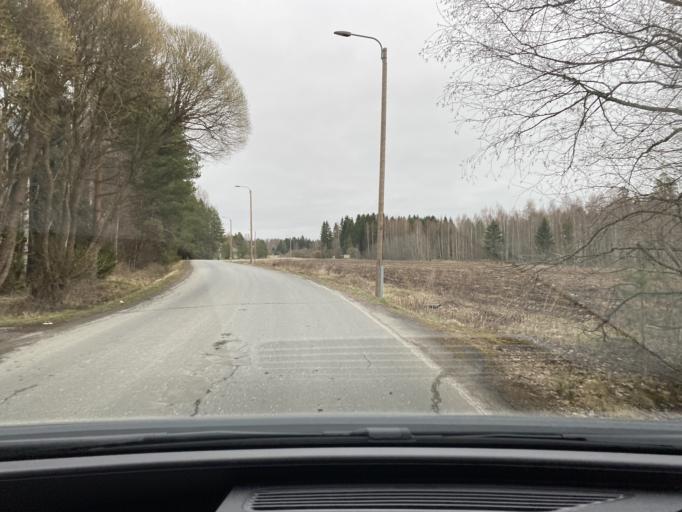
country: FI
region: Satakunta
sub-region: Pori
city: Huittinen
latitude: 61.1659
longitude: 22.7228
